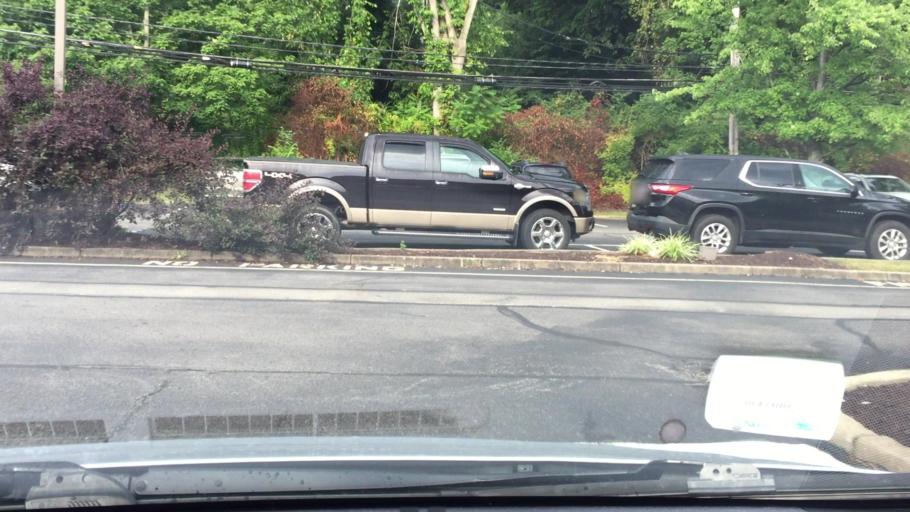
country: US
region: Pennsylvania
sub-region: Allegheny County
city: Enlow
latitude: 40.4594
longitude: -80.1923
